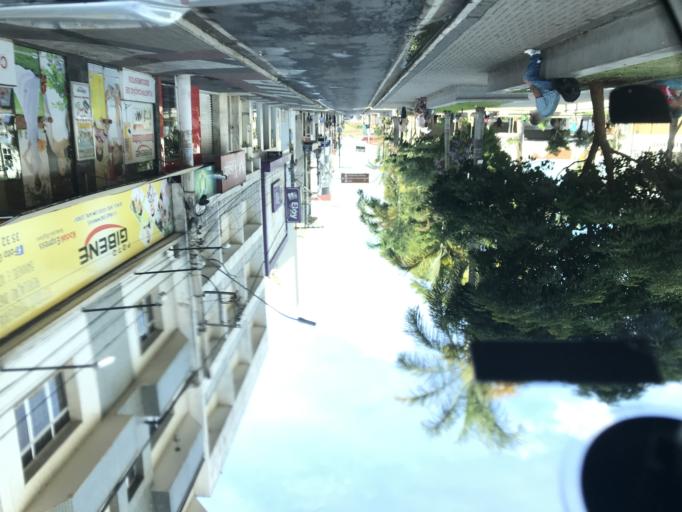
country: BR
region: Minas Gerais
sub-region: Tres Coracoes
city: Tres Coracoes
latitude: -21.6990
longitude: -45.2564
